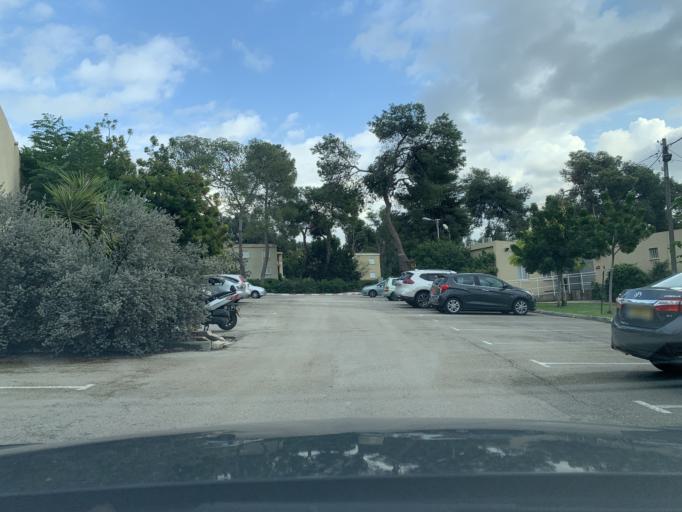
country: IL
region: Central District
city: Rosh Ha'Ayin
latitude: 32.0621
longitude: 34.9510
